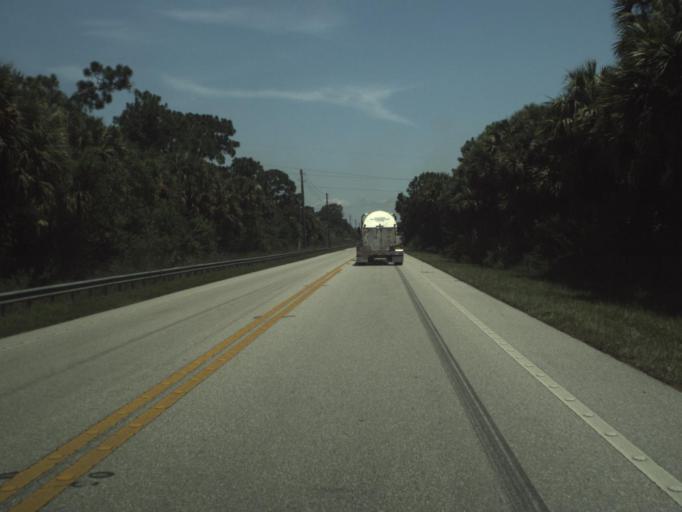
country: US
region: Florida
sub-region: Martin County
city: Indiantown
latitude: 27.0961
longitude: -80.5823
